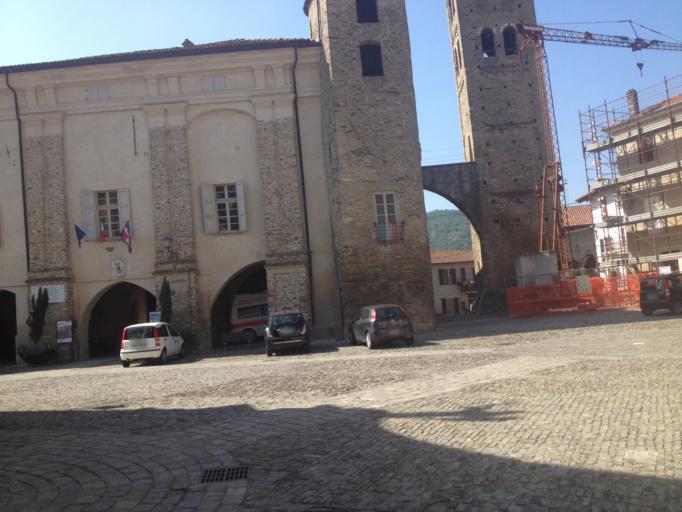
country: IT
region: Piedmont
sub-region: Provincia di Asti
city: Monastero Bormida
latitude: 44.6479
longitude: 8.3251
